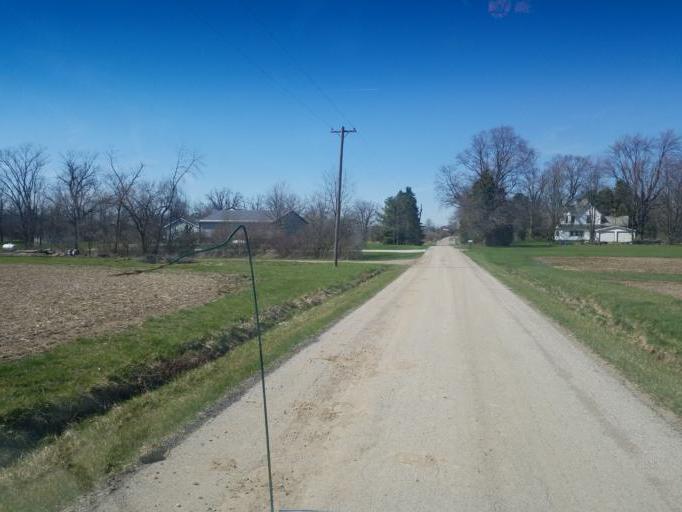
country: US
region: Ohio
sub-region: Morrow County
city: Cardington
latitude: 40.5450
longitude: -82.9132
